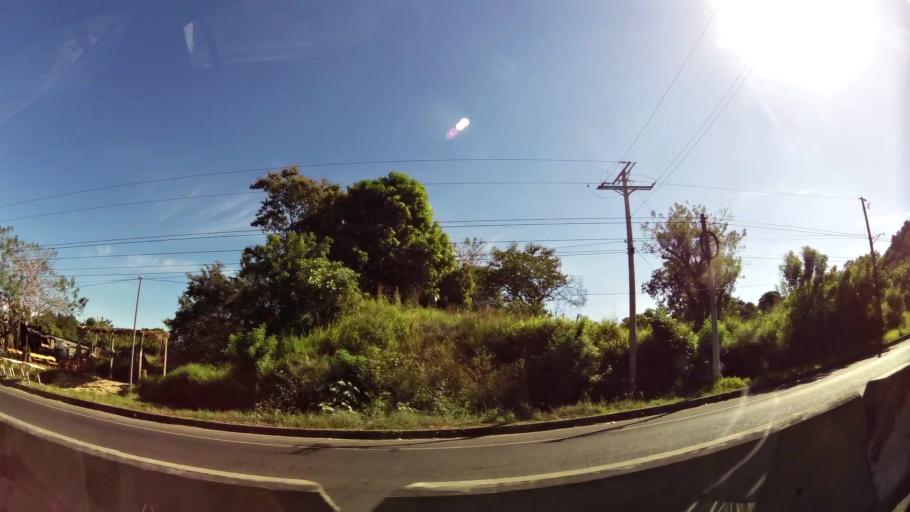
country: SV
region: Santa Ana
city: Coatepeque
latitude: 13.9253
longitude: -89.5202
